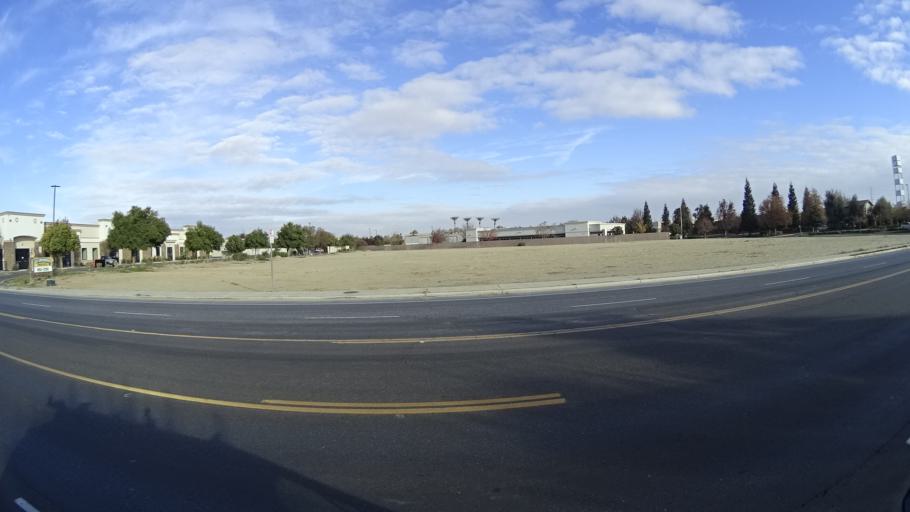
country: US
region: California
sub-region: Kern County
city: Greenacres
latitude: 35.3032
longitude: -119.0995
